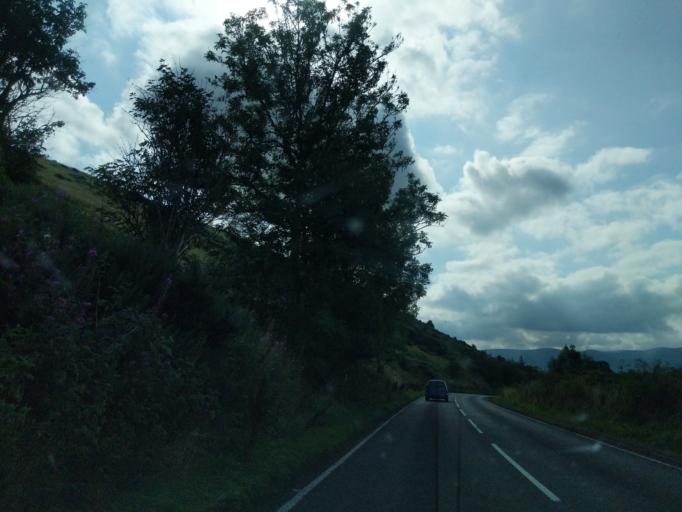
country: GB
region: Scotland
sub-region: The Scottish Borders
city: Peebles
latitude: 55.6811
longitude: -3.2070
